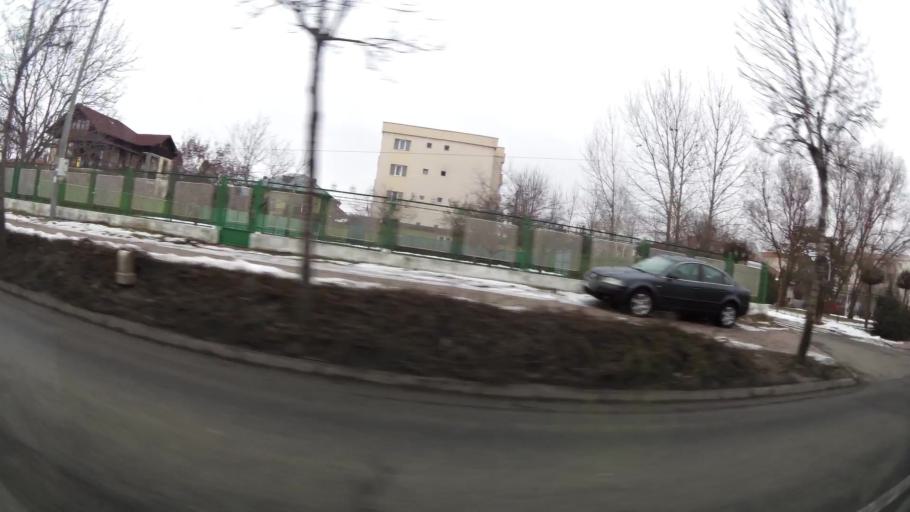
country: RO
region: Ilfov
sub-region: Comuna Chitila
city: Chitila
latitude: 44.5070
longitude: 25.9841
